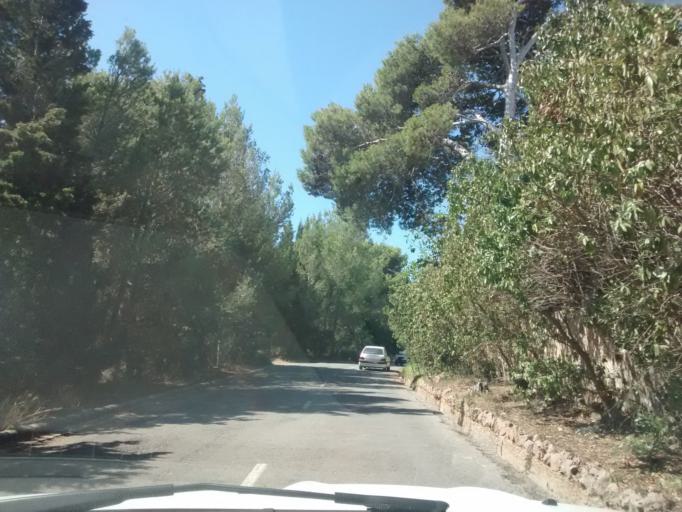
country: ES
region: Balearic Islands
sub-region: Illes Balears
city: Port d'Alcudia
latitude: 39.8699
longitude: 3.1521
